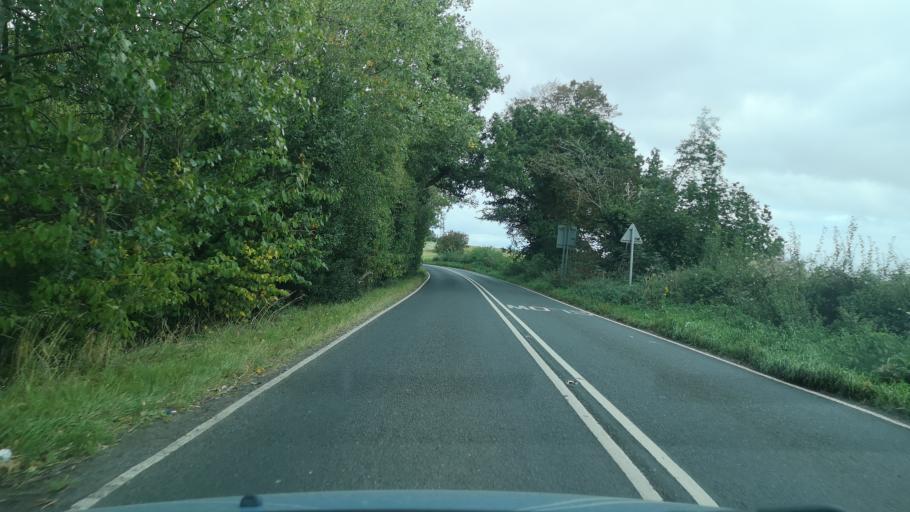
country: GB
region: England
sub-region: City and Borough of Wakefield
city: Walton
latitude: 53.6404
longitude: -1.4796
